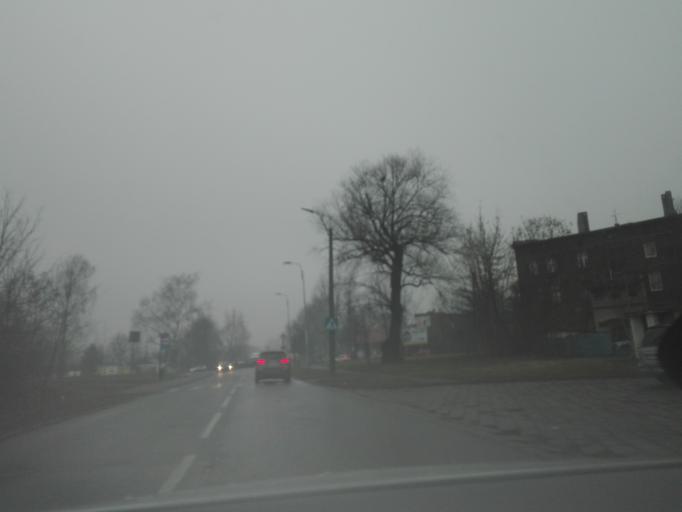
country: PL
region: Silesian Voivodeship
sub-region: Katowice
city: Katowice
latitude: 50.2732
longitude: 19.0530
